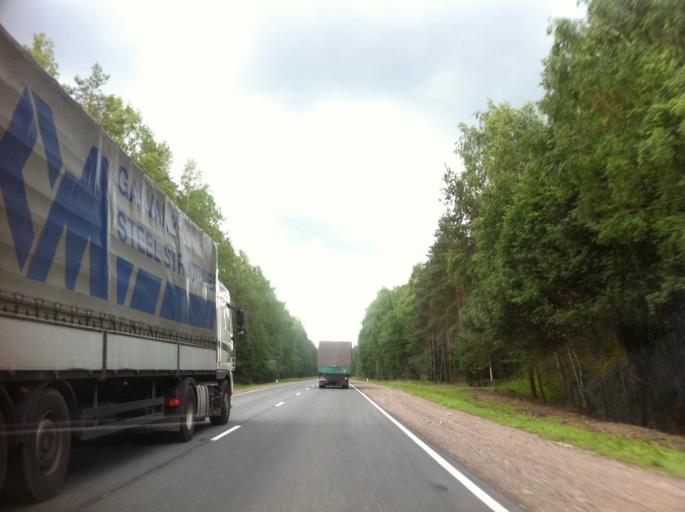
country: RU
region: Pskov
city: Pskov
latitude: 57.8718
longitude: 28.5536
